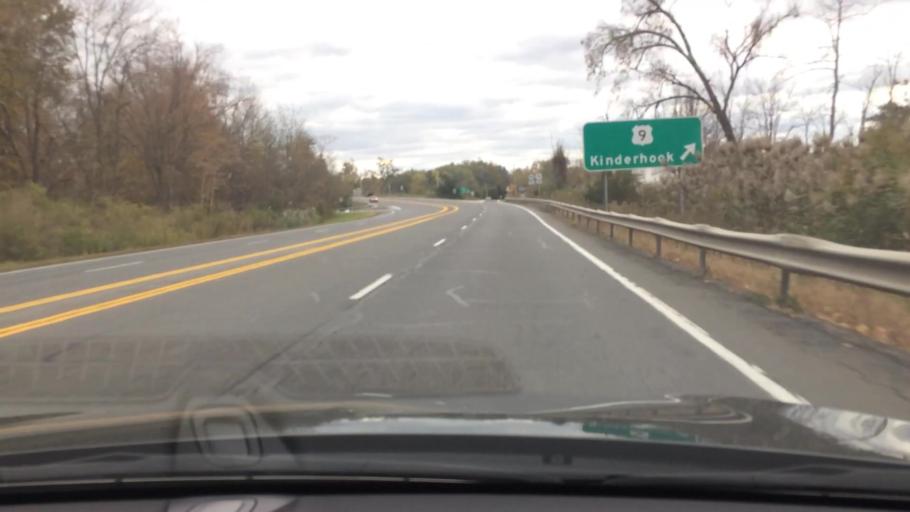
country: US
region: New York
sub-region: Columbia County
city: Kinderhook
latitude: 42.4108
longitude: -73.6913
